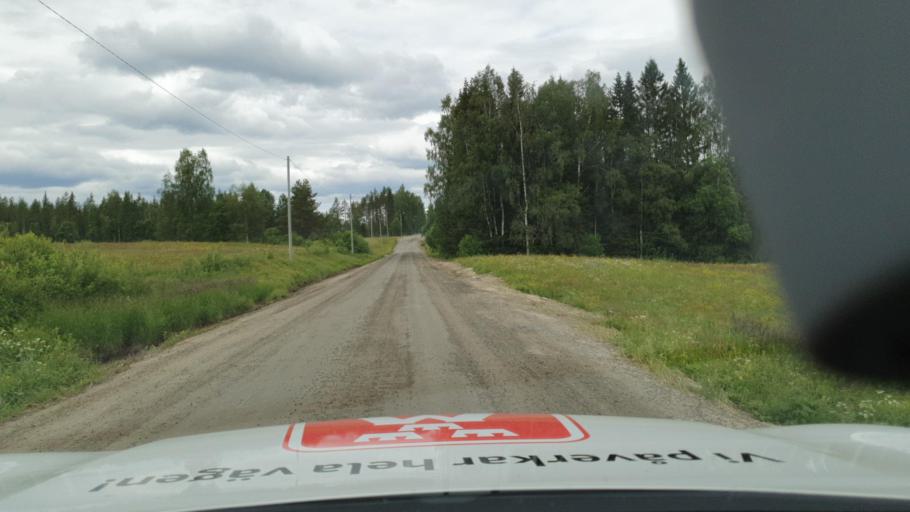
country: SE
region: Vaesterbotten
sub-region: Nordmalings Kommun
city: Nordmaling
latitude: 63.7158
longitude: 19.4280
